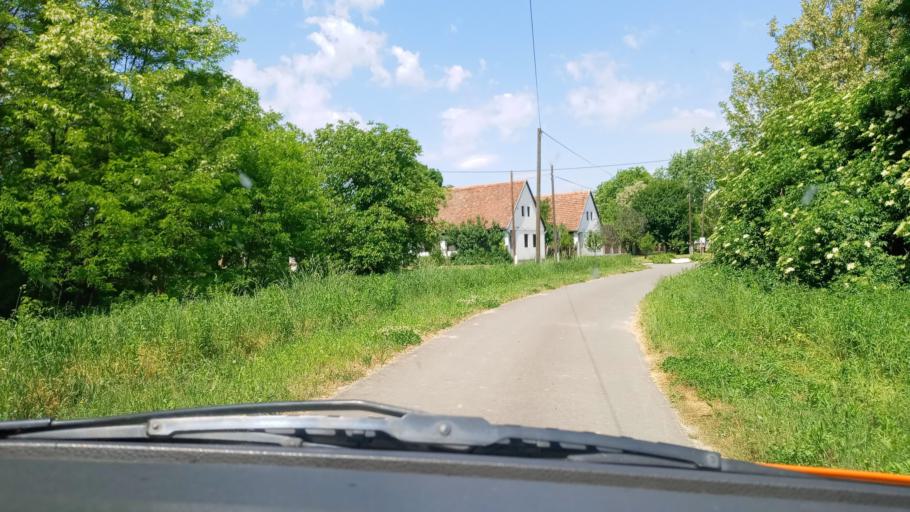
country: HR
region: Osjecko-Baranjska
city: Viljevo
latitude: 45.8087
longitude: 18.1165
